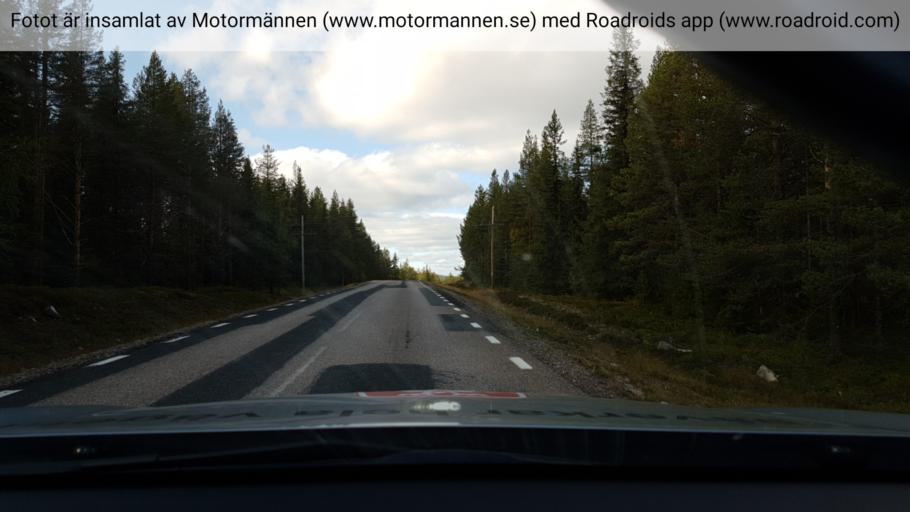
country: SE
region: Vaesterbotten
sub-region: Mala Kommun
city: Mala
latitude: 65.4418
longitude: 18.4301
